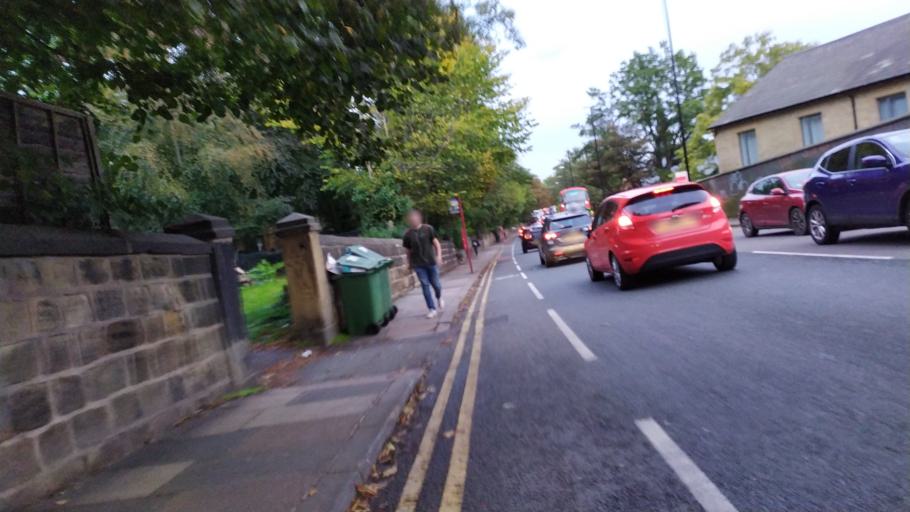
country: GB
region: England
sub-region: City and Borough of Leeds
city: Leeds
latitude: 53.8164
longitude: -1.5666
